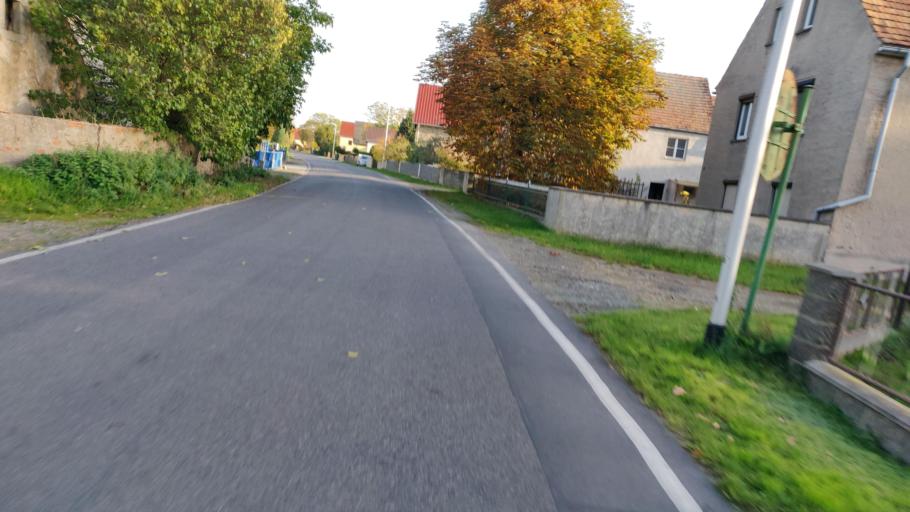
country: DE
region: Saxony
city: Zabeltitz
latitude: 51.3411
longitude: 13.5583
